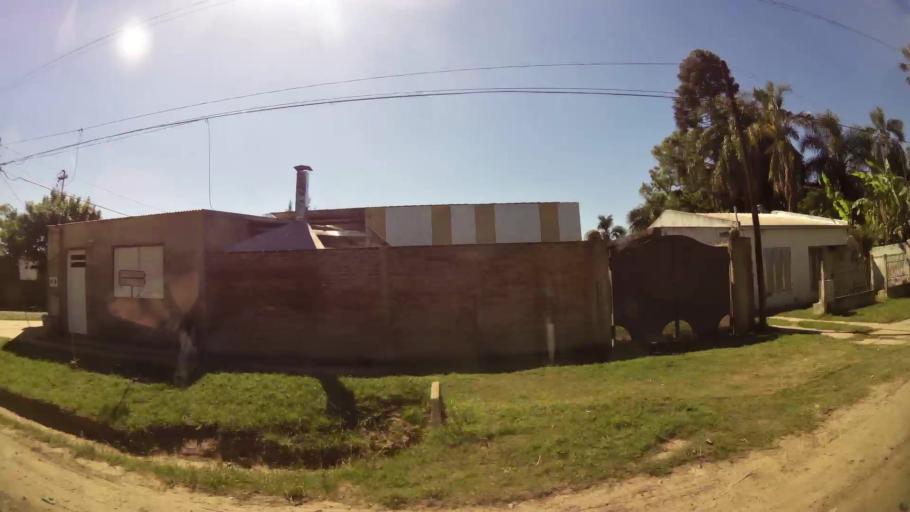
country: AR
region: Santa Fe
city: Esperanza
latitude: -31.4622
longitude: -60.9323
